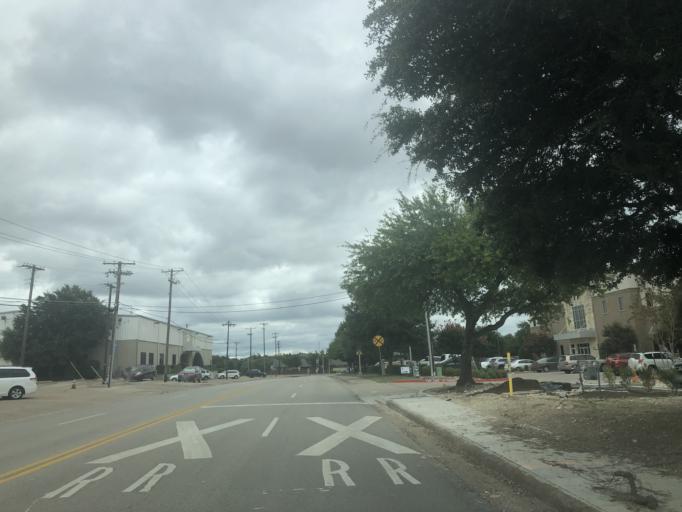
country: US
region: Texas
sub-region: Dallas County
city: Duncanville
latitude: 32.6421
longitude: -96.9213
